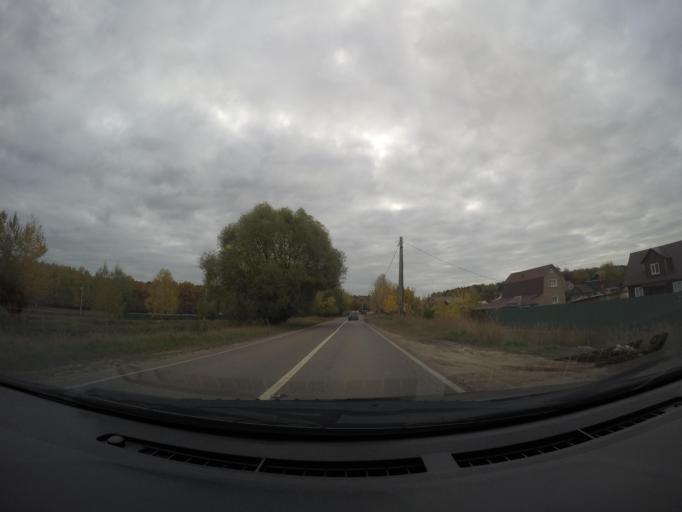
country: RU
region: Moskovskaya
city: Gzhel'
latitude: 55.6261
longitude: 38.4362
